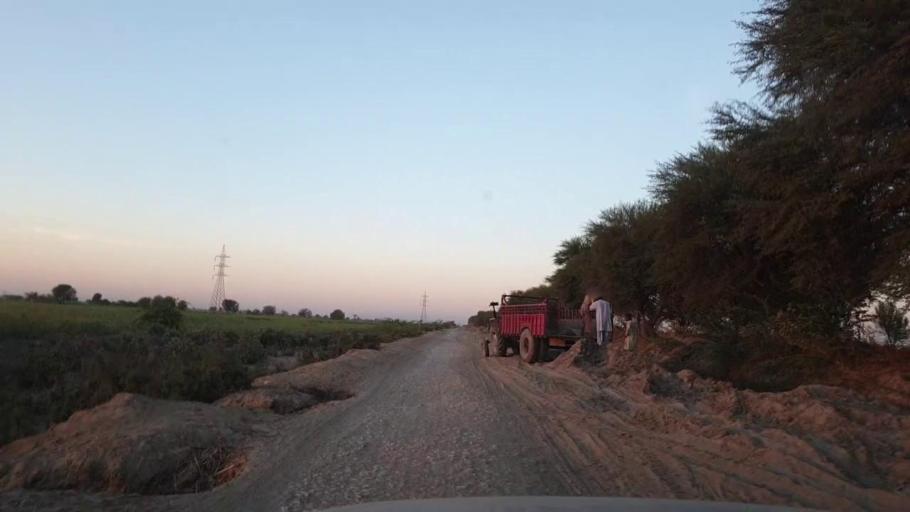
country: PK
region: Sindh
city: Kunri
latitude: 25.1485
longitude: 69.4462
